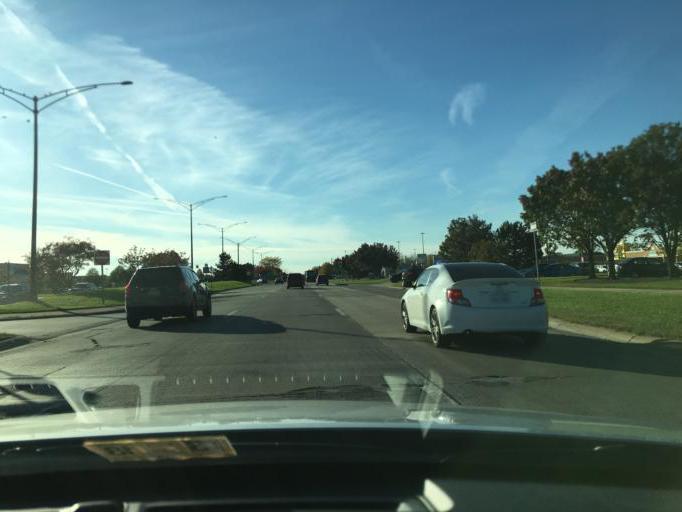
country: US
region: Michigan
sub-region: Oakland County
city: Clawson
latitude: 42.5637
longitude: -83.1082
